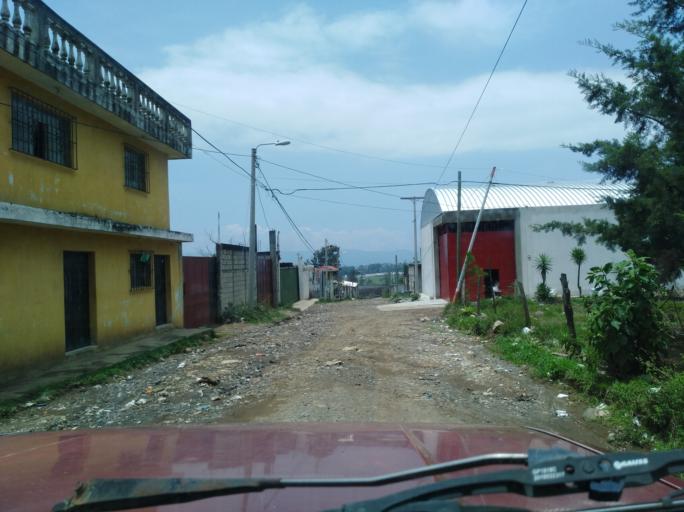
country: GT
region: Guatemala
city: Villa Nueva
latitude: 14.5275
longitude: -90.6212
